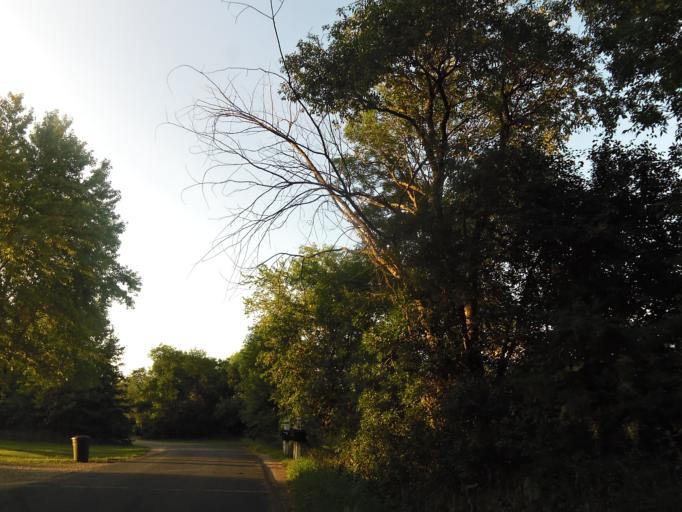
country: US
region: Minnesota
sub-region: Washington County
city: Stillwater
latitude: 45.0631
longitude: -92.7890
